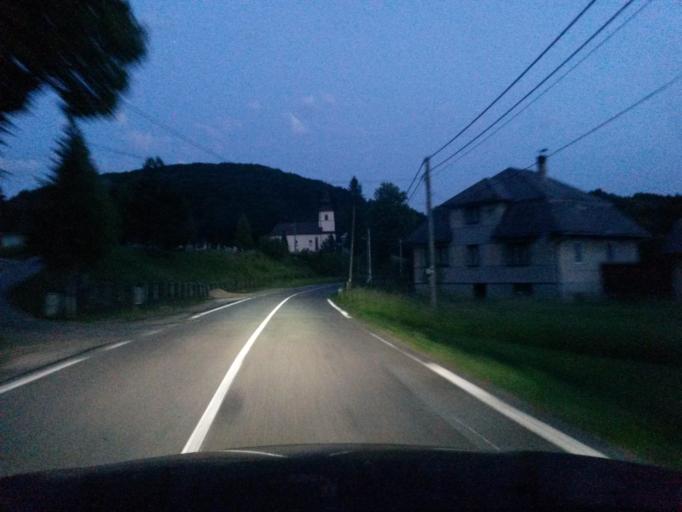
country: UA
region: Zakarpattia
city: Velykyi Bereznyi
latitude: 48.9236
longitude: 22.3177
